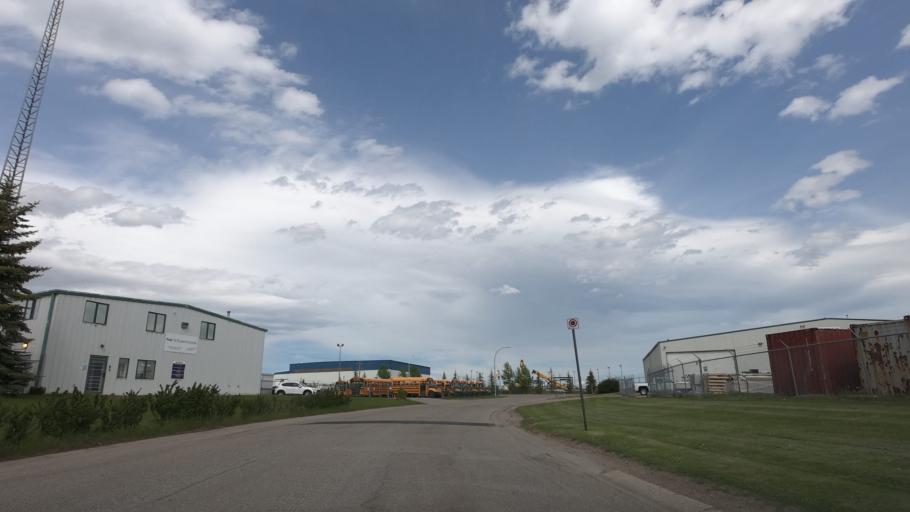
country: CA
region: Alberta
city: Airdrie
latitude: 51.2917
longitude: -113.9825
